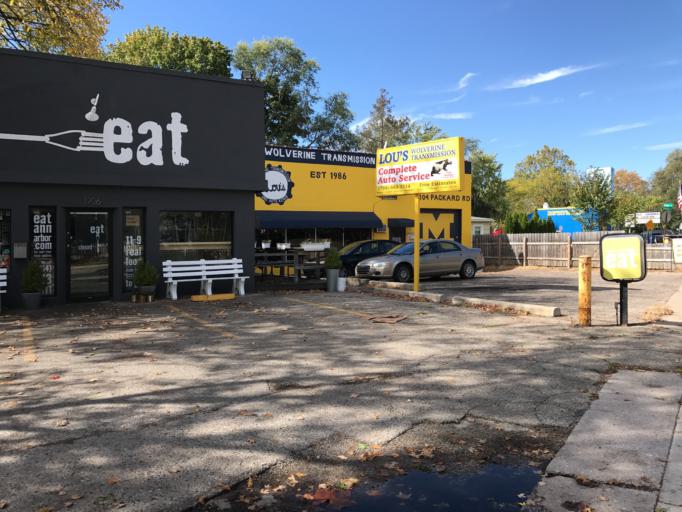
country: US
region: Michigan
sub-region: Washtenaw County
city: Ann Arbor
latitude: 42.2586
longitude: -83.7285
